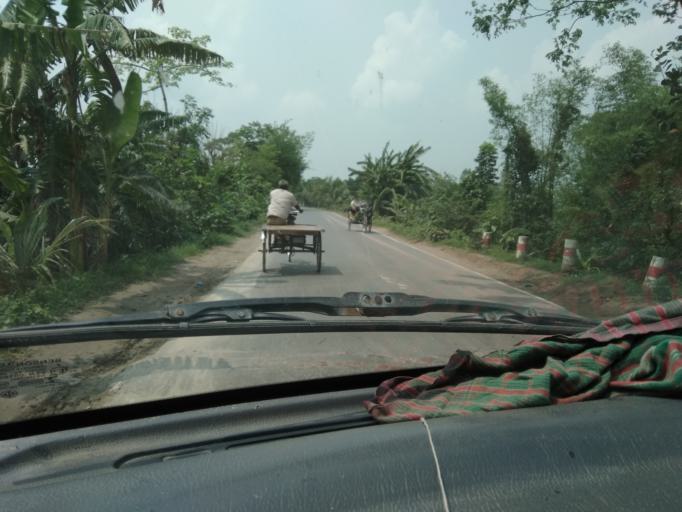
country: BD
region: Dhaka
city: Char Bhadrasan
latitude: 23.4026
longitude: 90.2190
